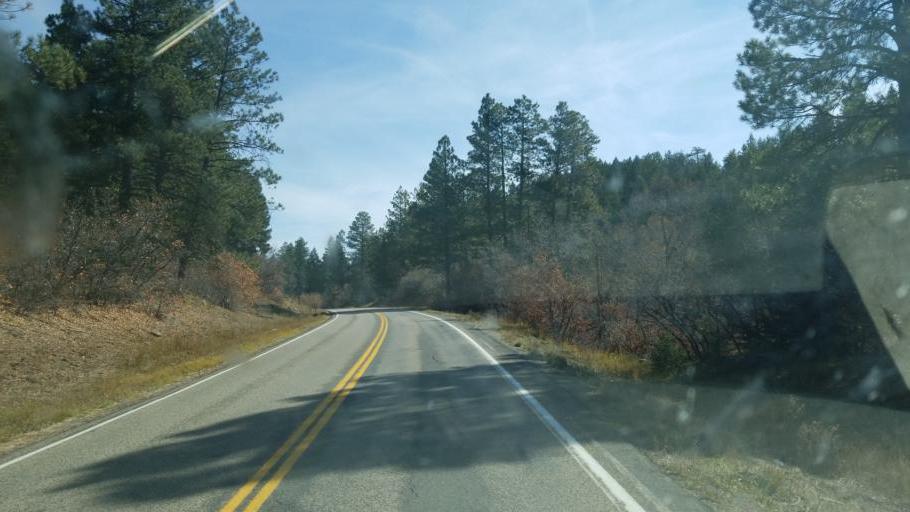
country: US
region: New Mexico
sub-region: Rio Arriba County
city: Dulce
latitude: 37.0753
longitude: -106.8472
